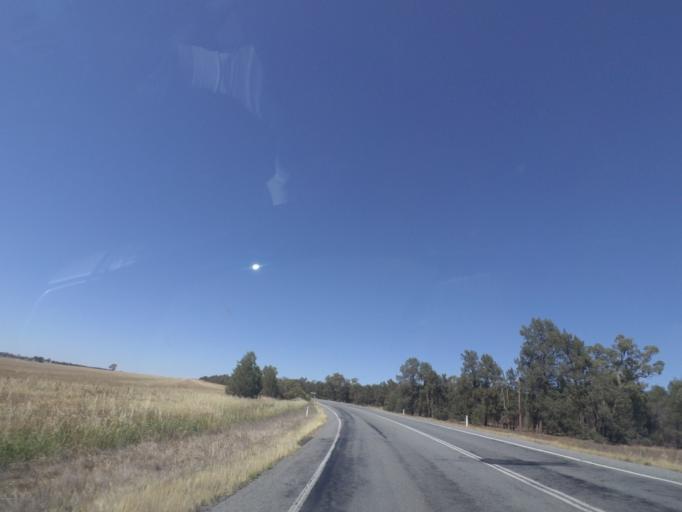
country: AU
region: New South Wales
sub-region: Narrandera
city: Narrandera
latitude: -34.4207
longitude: 146.8460
